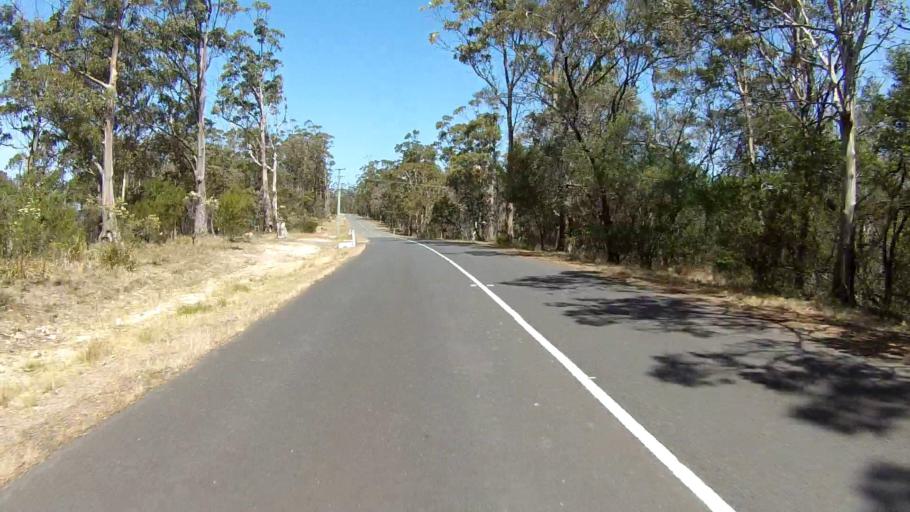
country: AU
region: Tasmania
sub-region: Clarence
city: Sandford
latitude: -43.0133
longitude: 147.4806
